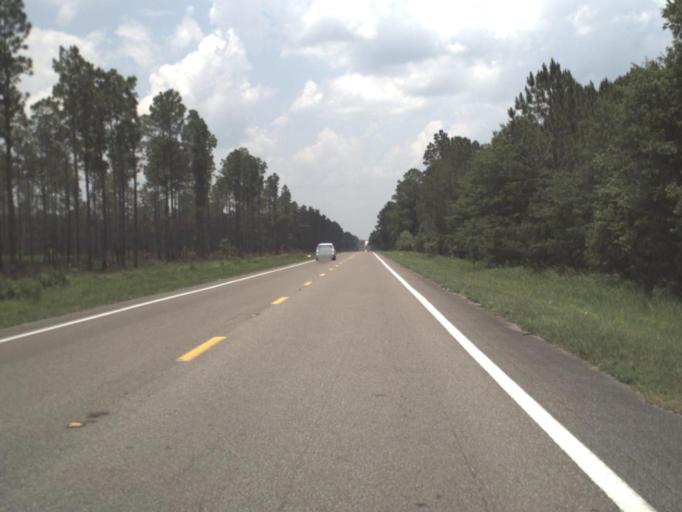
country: US
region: Florida
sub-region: Putnam County
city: Palatka
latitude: 29.5074
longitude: -81.7485
